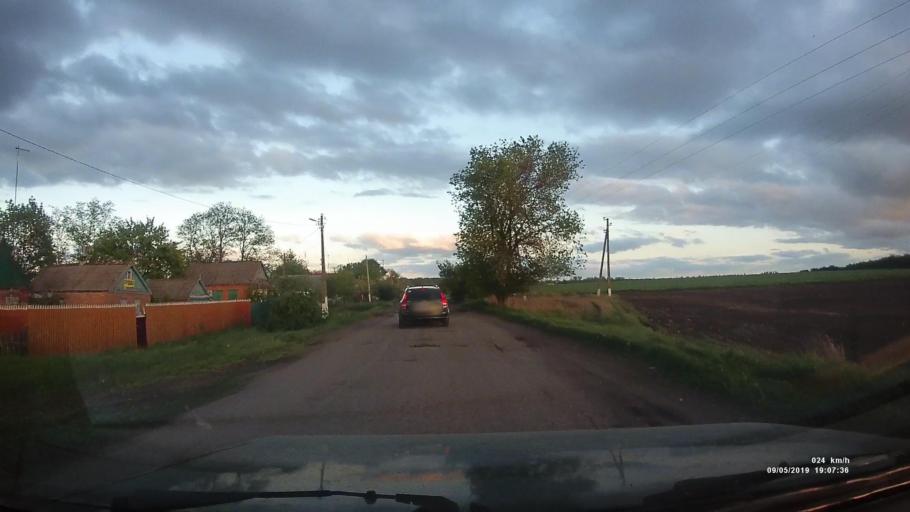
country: RU
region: Krasnodarskiy
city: Kanelovskaya
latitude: 46.7335
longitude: 39.1982
